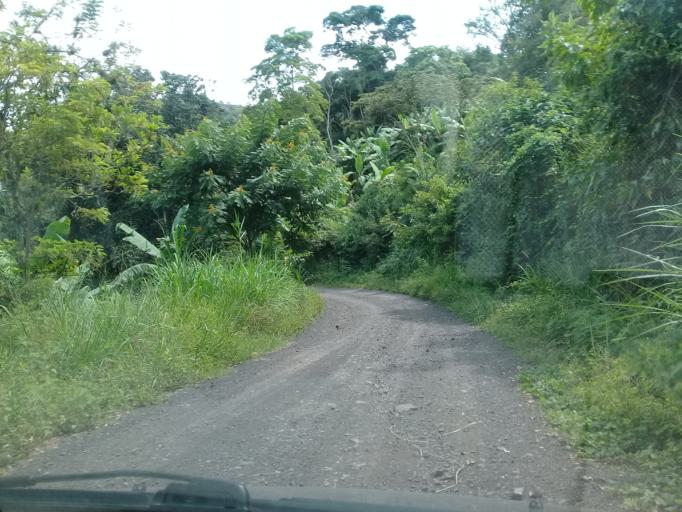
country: CO
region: Cundinamarca
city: Viani
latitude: 4.8541
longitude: -74.5444
